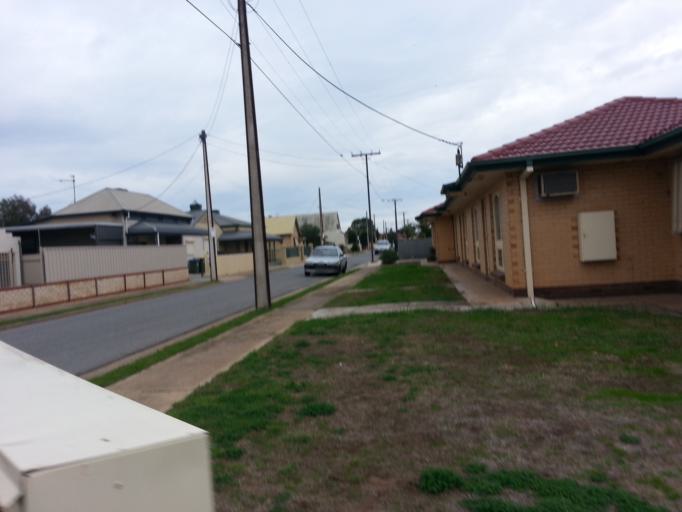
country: AU
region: South Australia
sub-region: Port Adelaide Enfield
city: Alberton
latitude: -34.8505
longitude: 138.5216
